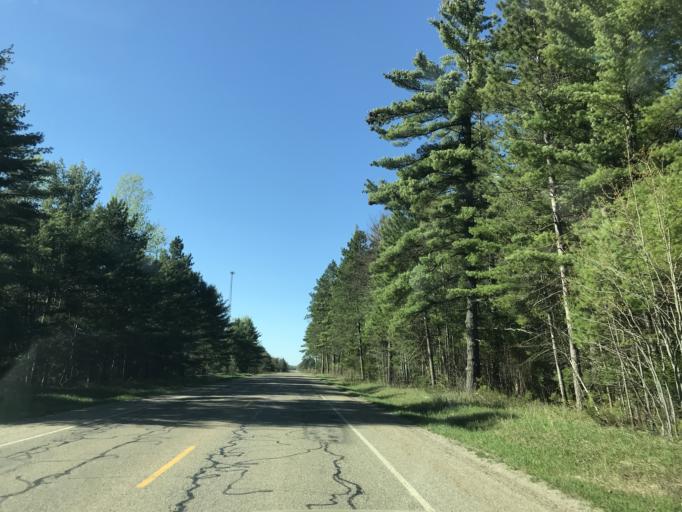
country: US
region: Michigan
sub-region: Crawford County
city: Grayling
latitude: 44.7357
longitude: -84.7495
